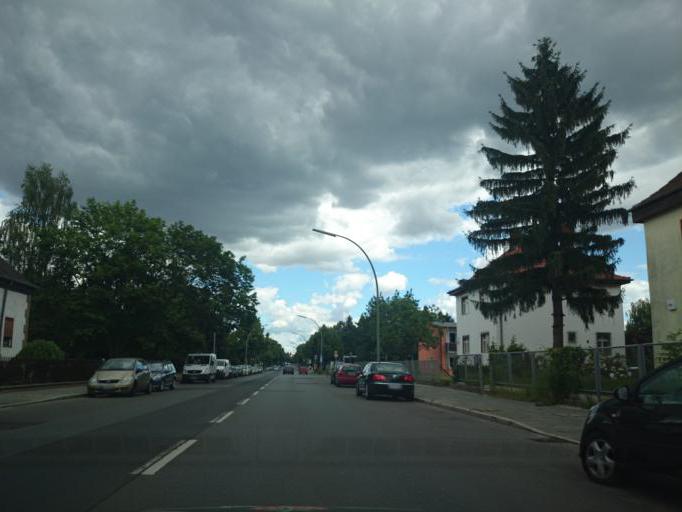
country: DE
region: Berlin
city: Marienfelde
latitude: 52.4161
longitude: 13.3655
